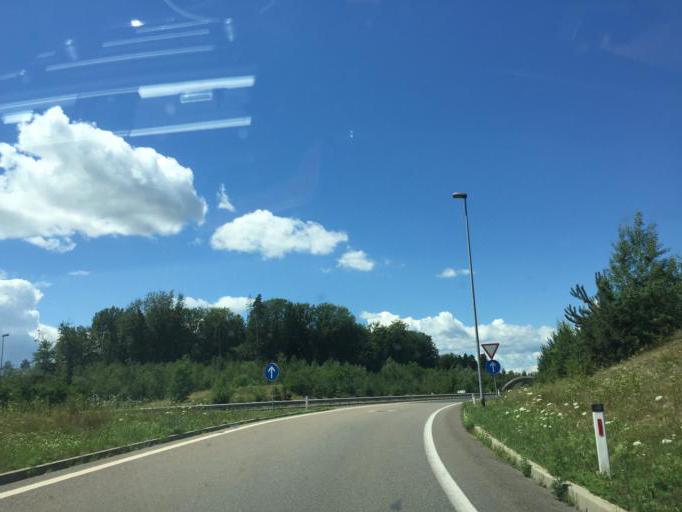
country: SI
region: Lenart
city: Lenart v Slov. Goricah
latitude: 46.5759
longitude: 15.8116
